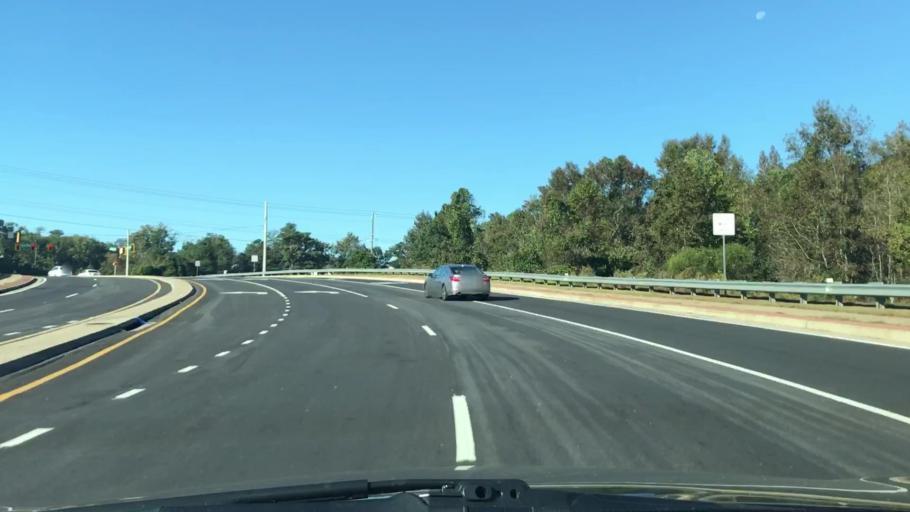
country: US
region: Georgia
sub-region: Douglas County
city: Douglasville
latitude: 33.7328
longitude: -84.7618
